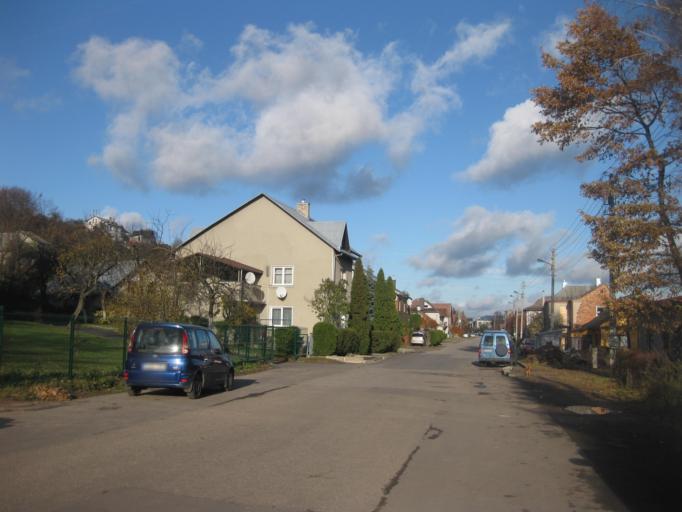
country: LT
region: Kauno apskritis
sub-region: Kaunas
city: Silainiai
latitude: 54.9208
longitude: 23.8959
